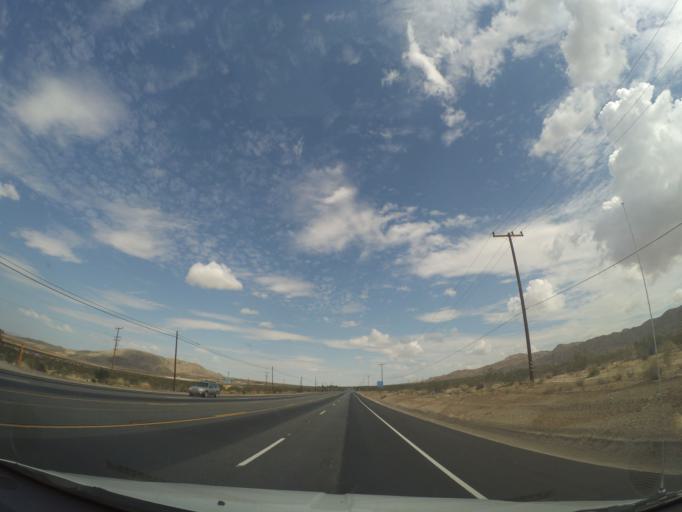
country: US
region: California
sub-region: San Bernardino County
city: Joshua Tree
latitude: 34.1352
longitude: -116.2337
